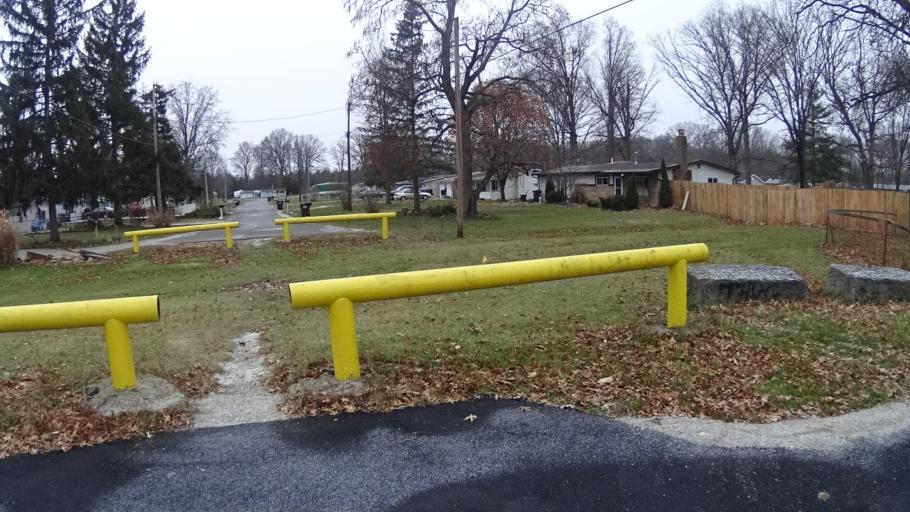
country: US
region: Ohio
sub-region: Lorain County
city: Eaton Estates
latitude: 41.3072
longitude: -82.0028
